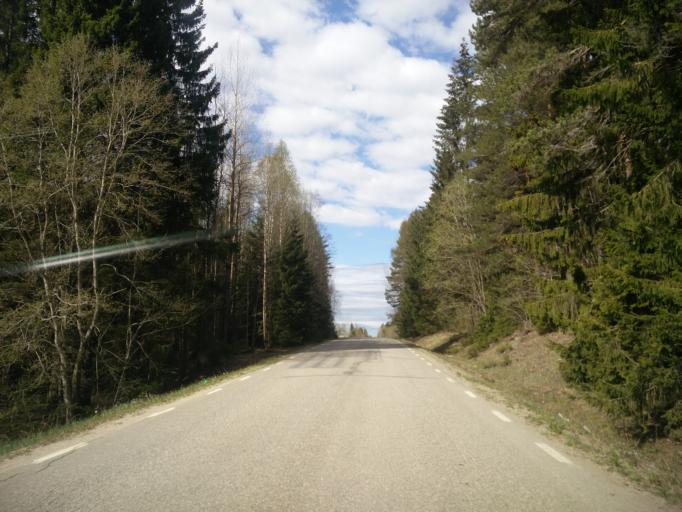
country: SE
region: Vaesternorrland
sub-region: Sundsvalls Kommun
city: Nolby
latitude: 62.2556
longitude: 17.3033
